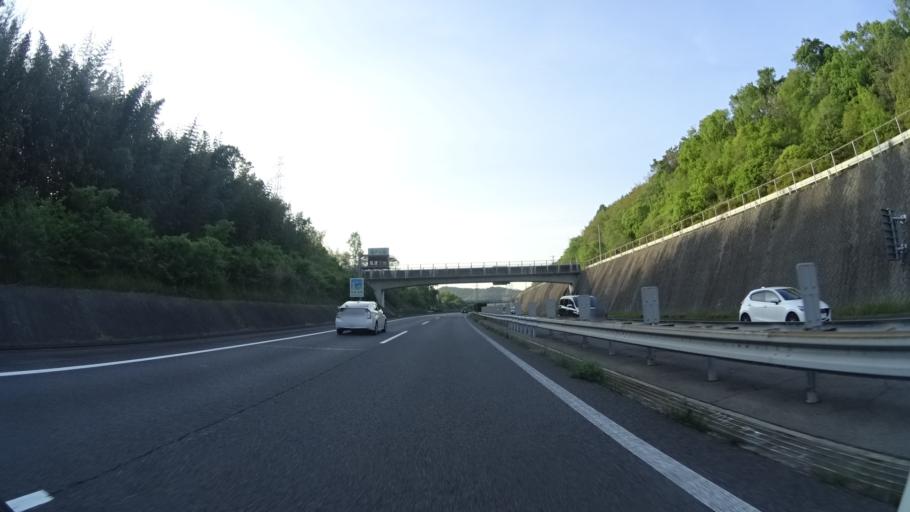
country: JP
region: Kagawa
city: Sakaidecho
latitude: 34.3037
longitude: 133.8407
